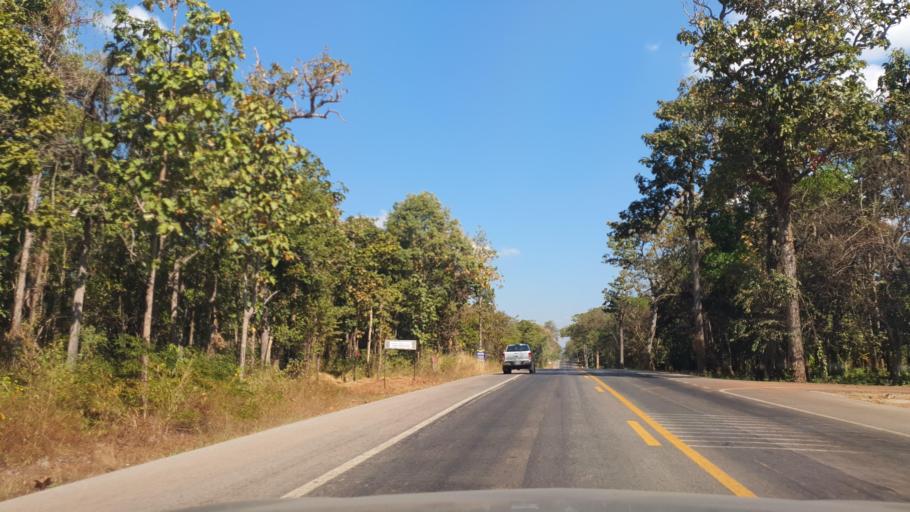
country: TH
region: Sakon Nakhon
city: Phu Phan
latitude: 16.9696
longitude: 103.9415
